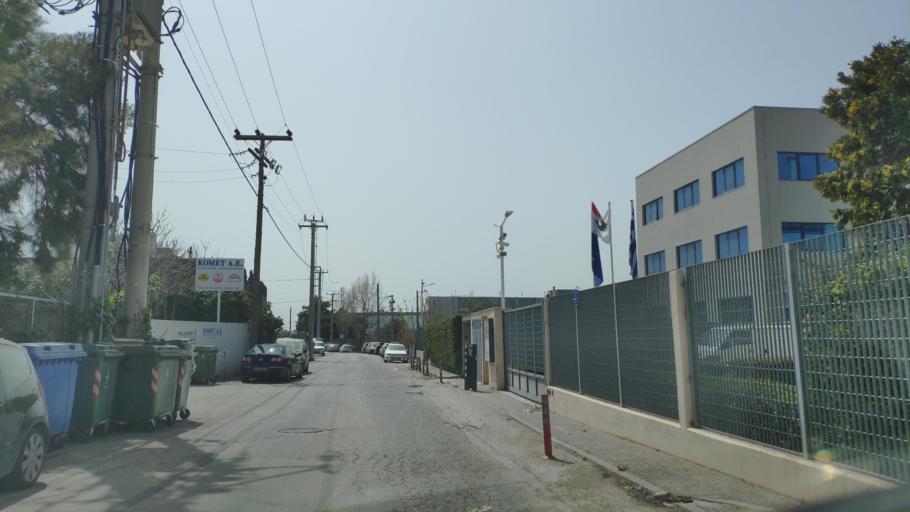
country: GR
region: Attica
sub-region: Nomarchia Athinas
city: Metamorfosi
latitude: 38.0755
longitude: 23.7690
